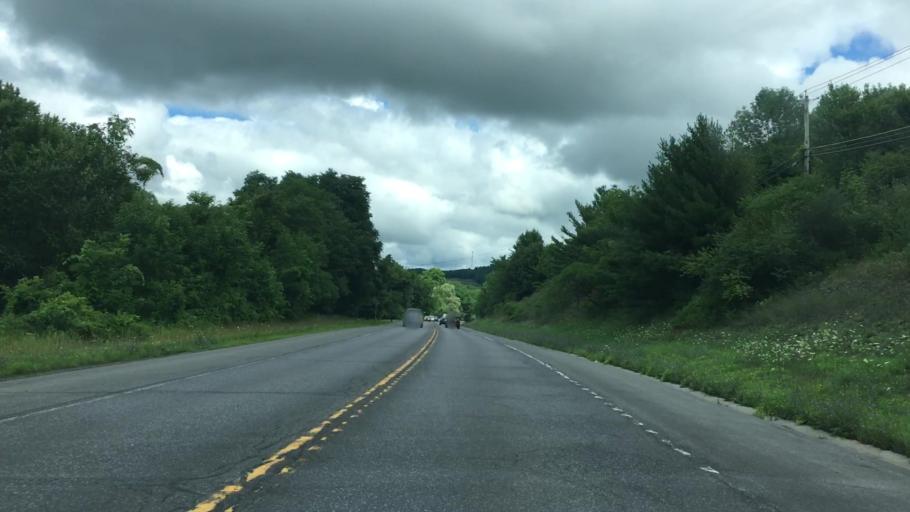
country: US
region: New York
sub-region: Rensselaer County
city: Poestenkill
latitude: 42.7914
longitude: -73.5703
